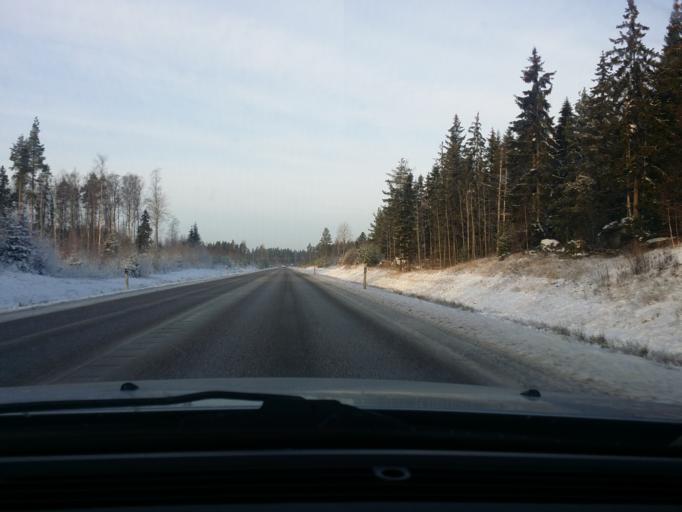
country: SE
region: OErebro
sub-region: Lindesbergs Kommun
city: Frovi
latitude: 59.4734
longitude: 15.3954
